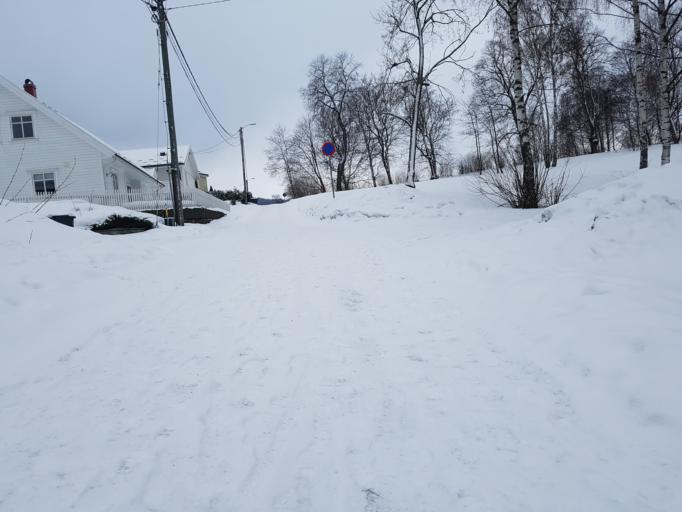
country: NO
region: Buskerud
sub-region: Drammen
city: Drammen
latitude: 59.7394
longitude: 10.1872
